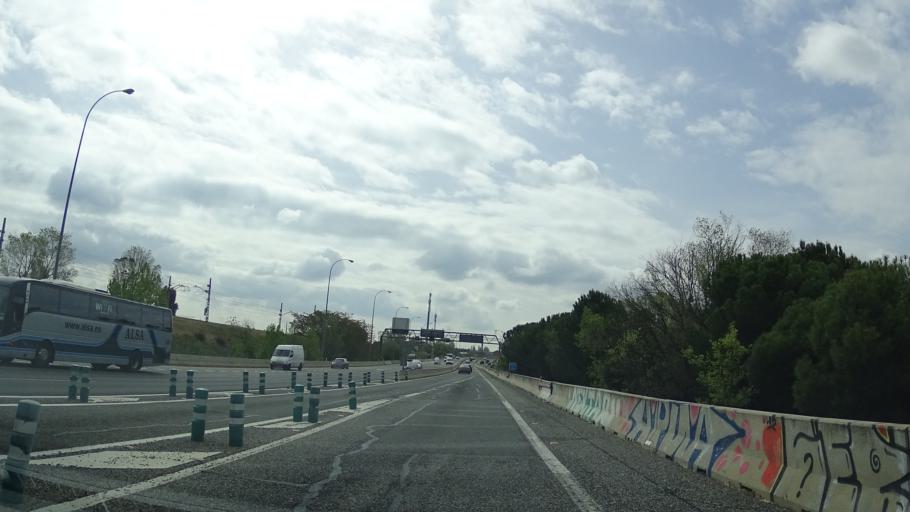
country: ES
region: Madrid
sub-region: Provincia de Madrid
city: Las Rozas de Madrid
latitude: 40.4982
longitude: -3.8717
